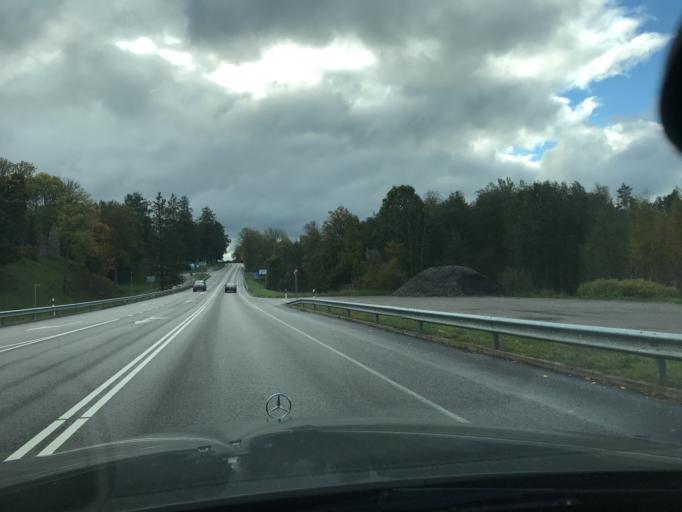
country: EE
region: Valgamaa
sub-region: Torva linn
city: Torva
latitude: 58.0177
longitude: 25.8769
